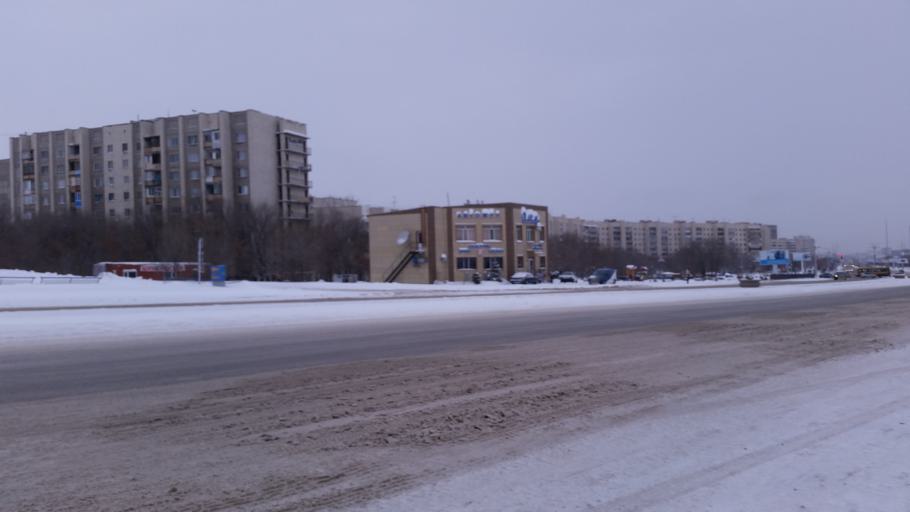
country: KZ
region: Qaraghandy
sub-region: Qaraghandy Qalasy
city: Karagandy
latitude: 49.7758
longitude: 73.1555
